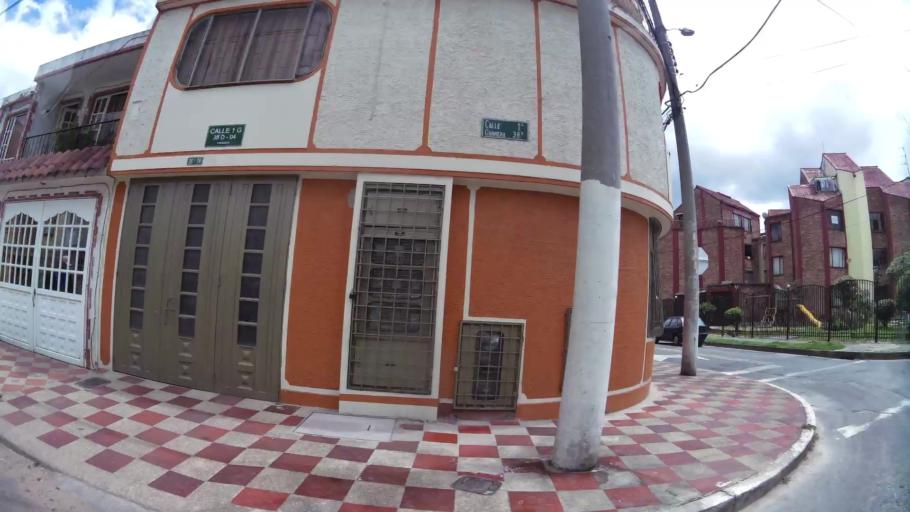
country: CO
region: Bogota D.C.
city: Bogota
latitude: 4.6078
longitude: -74.1124
